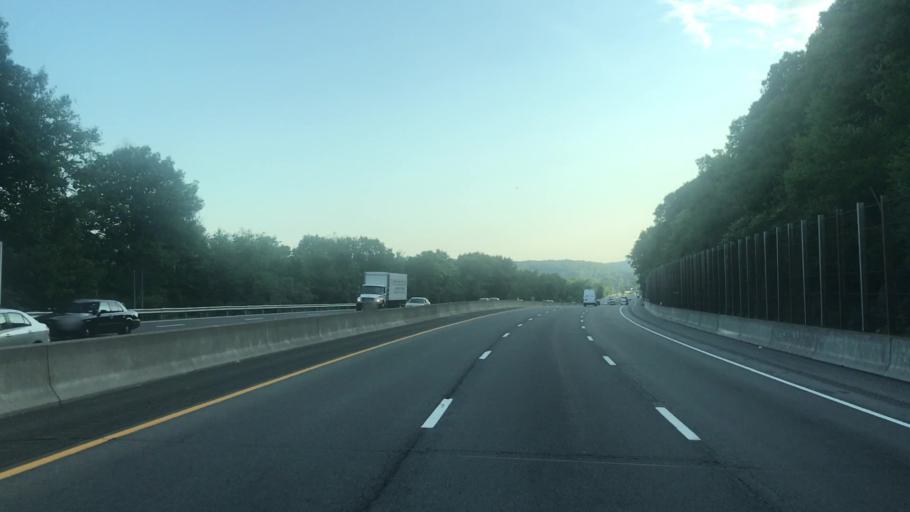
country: US
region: New York
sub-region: Westchester County
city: Ardsley
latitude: 40.9973
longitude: -73.8540
